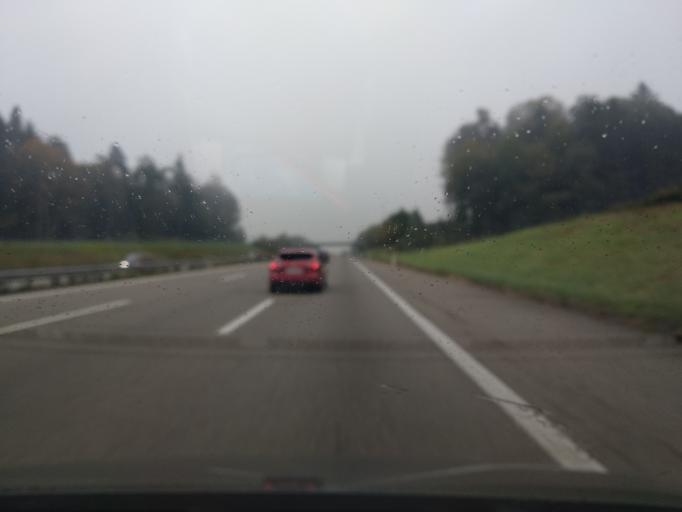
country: CH
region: Saint Gallen
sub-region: Wahlkreis Wil
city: Flawil
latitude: 47.4398
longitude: 9.1715
